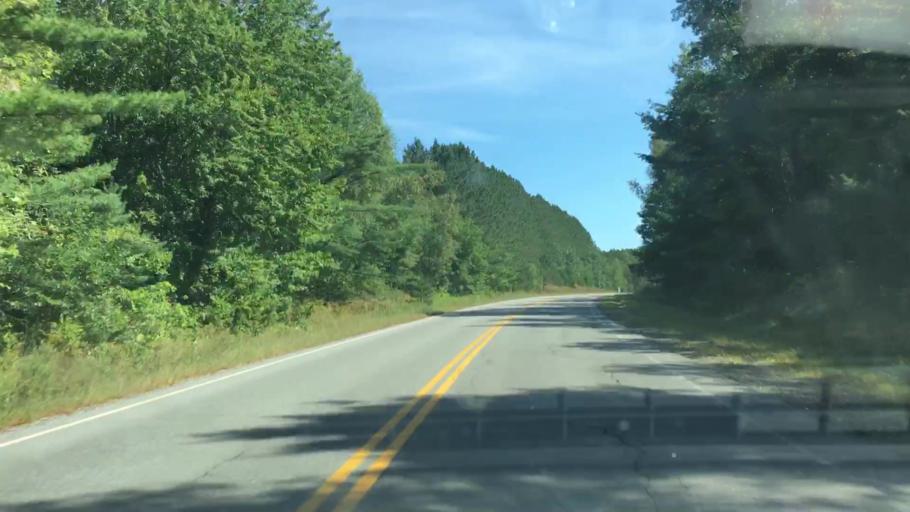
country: US
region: Maine
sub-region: Piscataquis County
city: Milo
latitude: 45.2294
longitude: -68.9349
